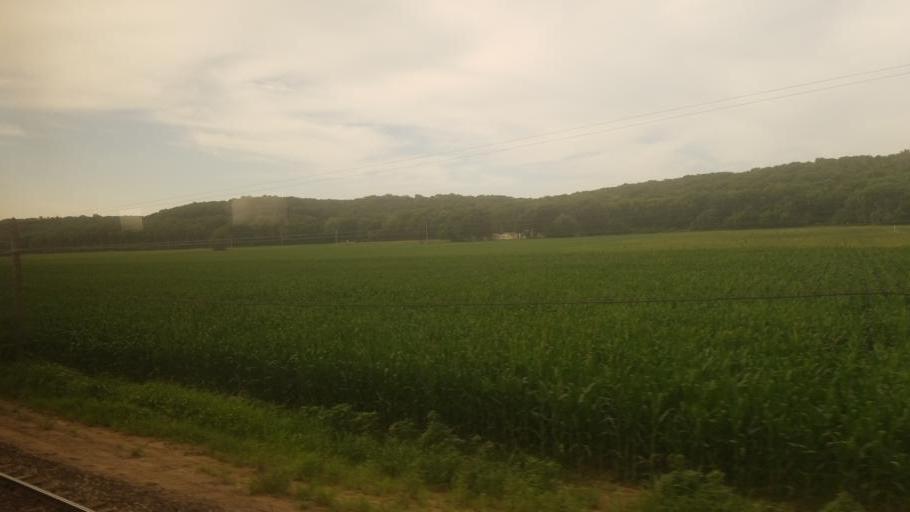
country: US
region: Kansas
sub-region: Shawnee County
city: Topeka
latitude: 39.0560
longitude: -95.5199
